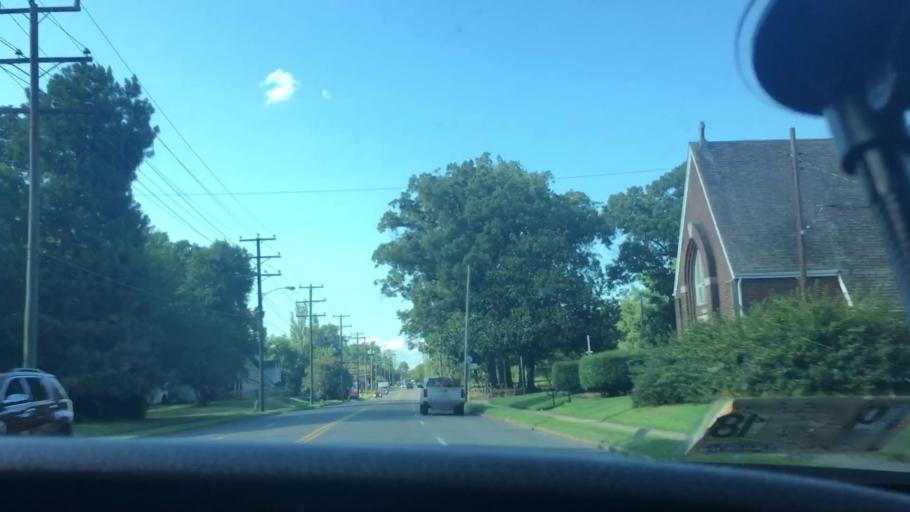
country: US
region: Virginia
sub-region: City of Chesapeake
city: Chesapeake
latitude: 36.8083
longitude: -76.2772
